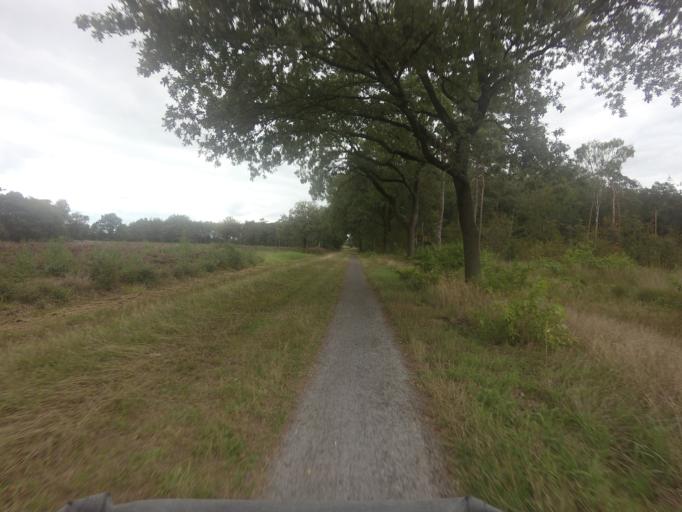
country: NL
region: Friesland
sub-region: Gemeente Weststellingwerf
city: Noordwolde
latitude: 52.9141
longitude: 6.2340
